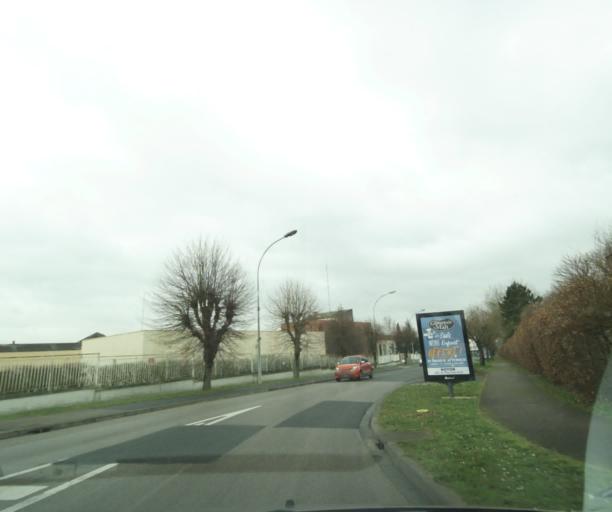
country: FR
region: Picardie
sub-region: Departement de l'Oise
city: Noyon
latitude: 49.5889
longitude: 3.0024
